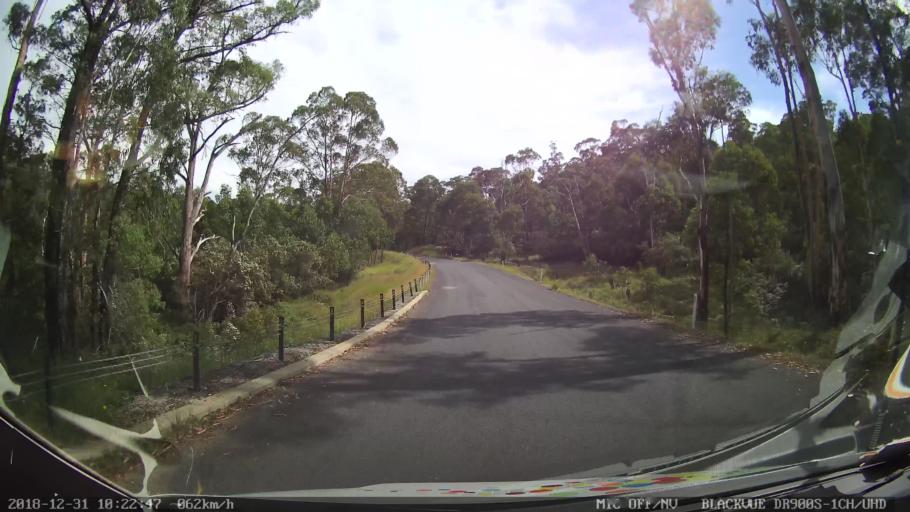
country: AU
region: New South Wales
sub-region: Snowy River
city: Jindabyne
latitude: -36.5226
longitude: 148.1433
